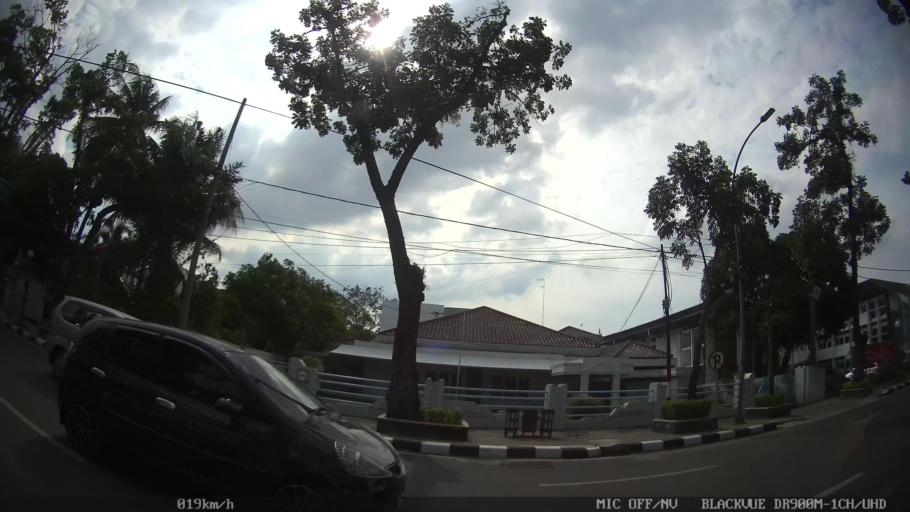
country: ID
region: North Sumatra
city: Medan
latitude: 3.5755
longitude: 98.6721
